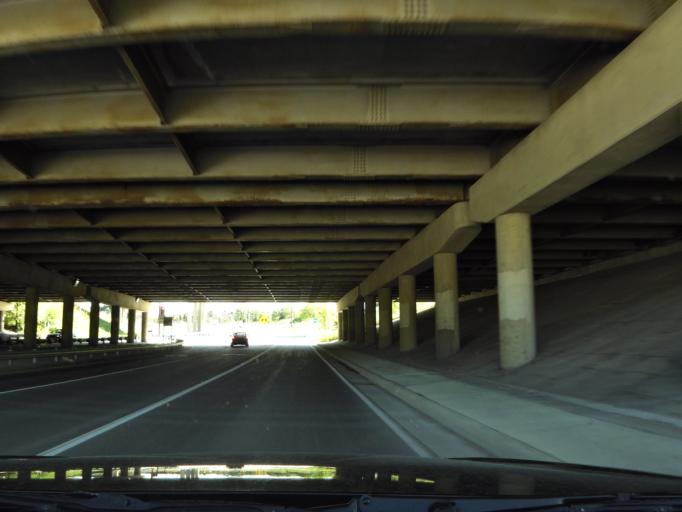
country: US
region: Minnesota
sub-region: Hennepin County
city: Minneapolis
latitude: 44.9722
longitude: -93.2519
